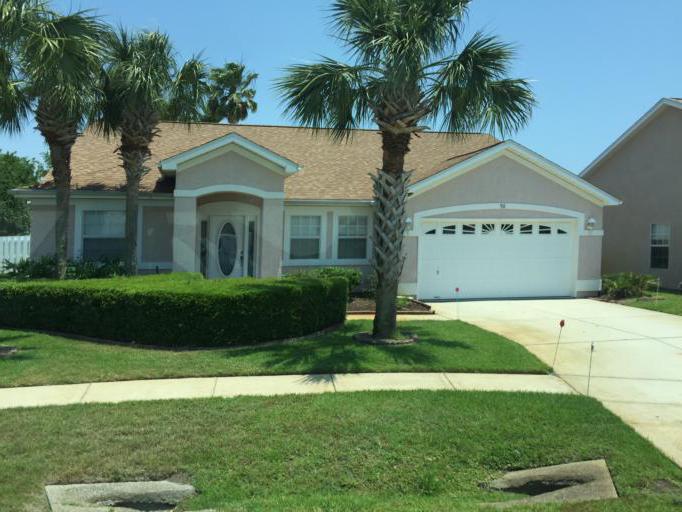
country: US
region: Florida
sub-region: Bay County
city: Laguna Beach
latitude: 30.2156
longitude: -85.8609
